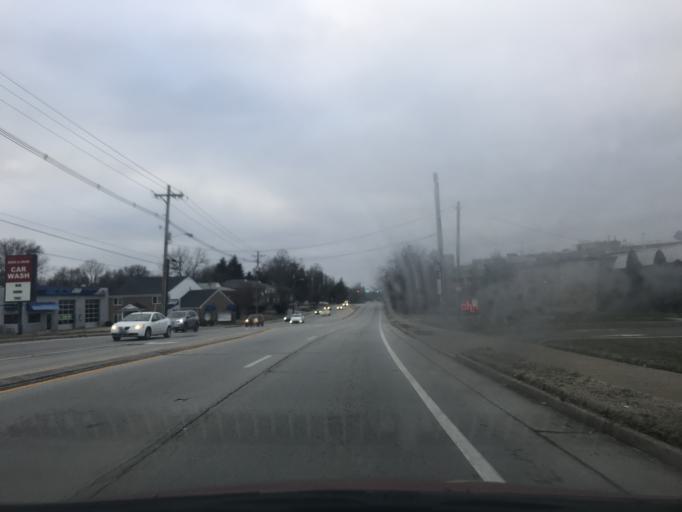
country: US
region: Kentucky
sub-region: Jefferson County
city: Audubon Park
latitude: 38.2123
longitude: -85.7212
